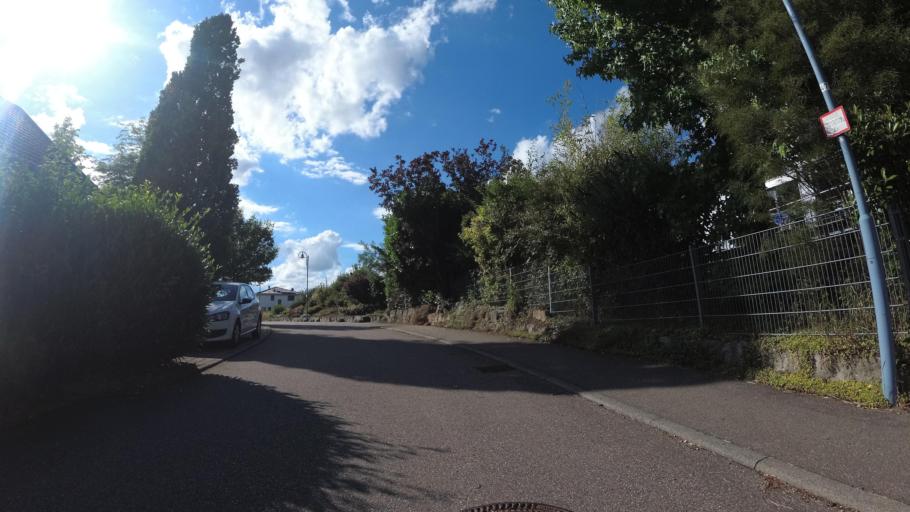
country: DE
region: Baden-Wuerttemberg
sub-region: Regierungsbezirk Stuttgart
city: Neuenstadt am Kocher
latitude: 49.2446
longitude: 9.3330
